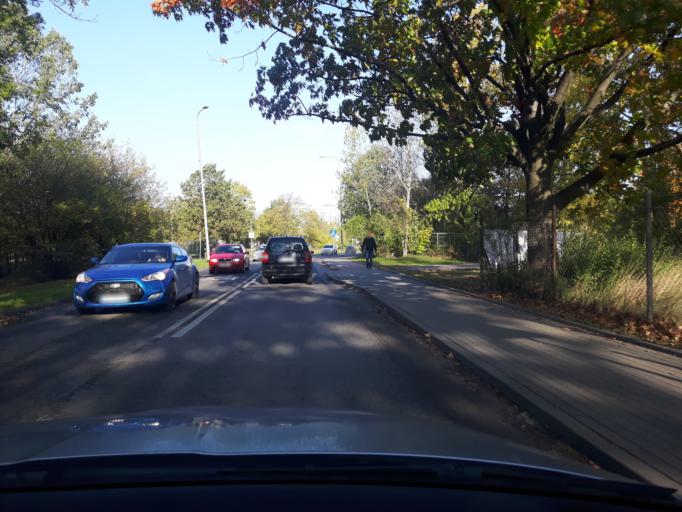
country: PL
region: Masovian Voivodeship
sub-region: Warszawa
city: Targowek
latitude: 52.2845
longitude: 21.0515
